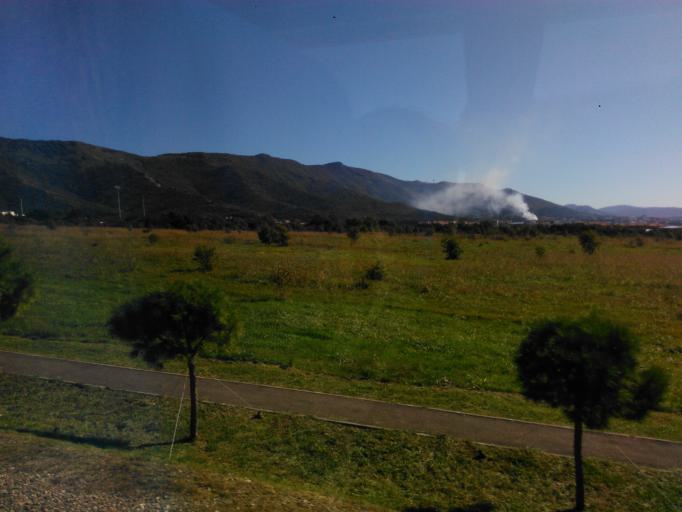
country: RU
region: Krasnodarskiy
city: Gelendzhik
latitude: 44.5955
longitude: 38.0274
